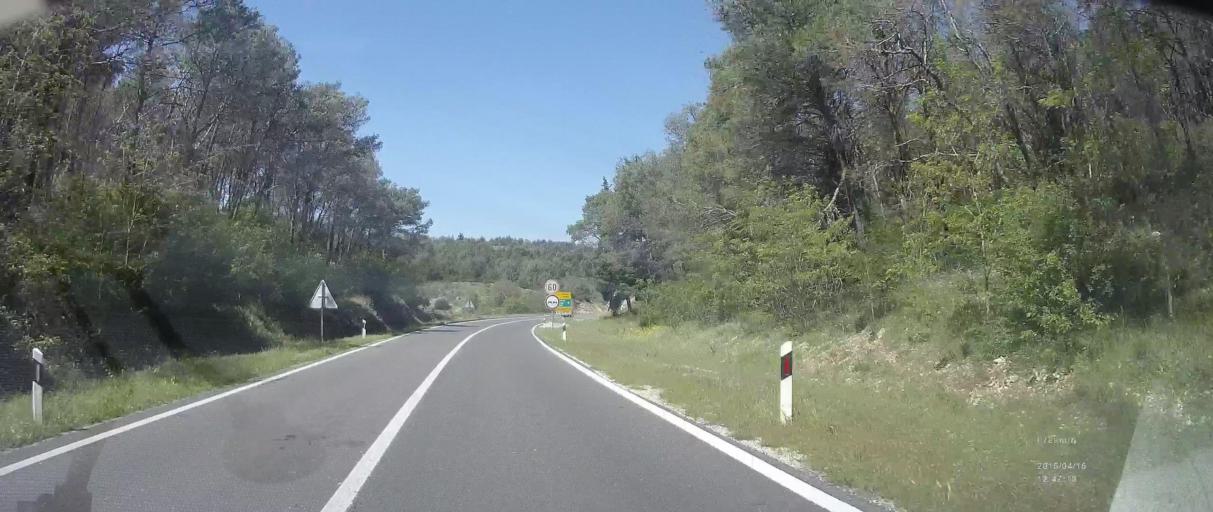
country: HR
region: Sibensko-Kniniska
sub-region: Grad Sibenik
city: Brodarica
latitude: 43.6612
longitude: 16.0489
